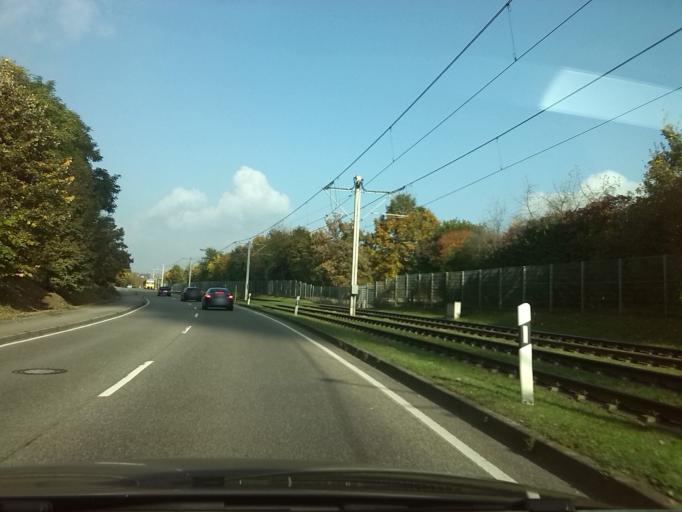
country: DE
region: Baden-Wuerttemberg
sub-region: Regierungsbezirk Stuttgart
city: Stuttgart Muehlhausen
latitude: 48.8497
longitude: 9.2439
